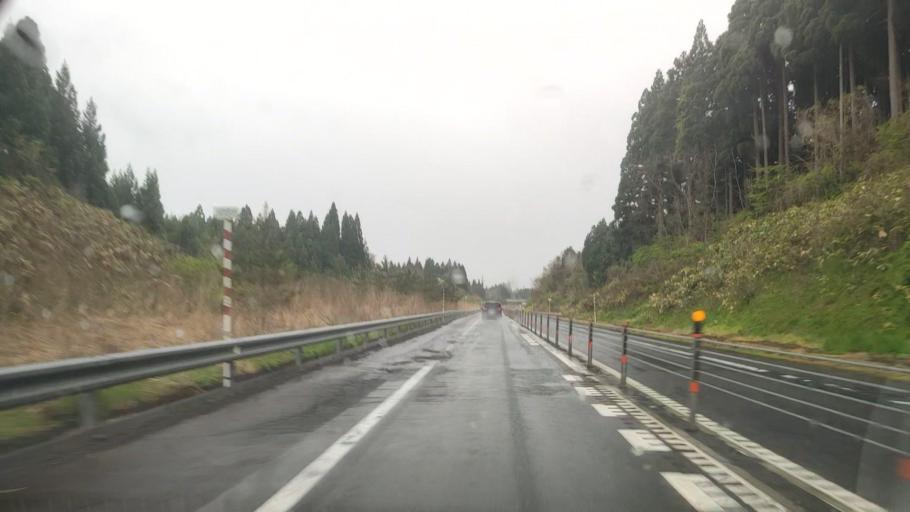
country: JP
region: Akita
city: Noshiromachi
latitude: 40.1724
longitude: 140.0539
